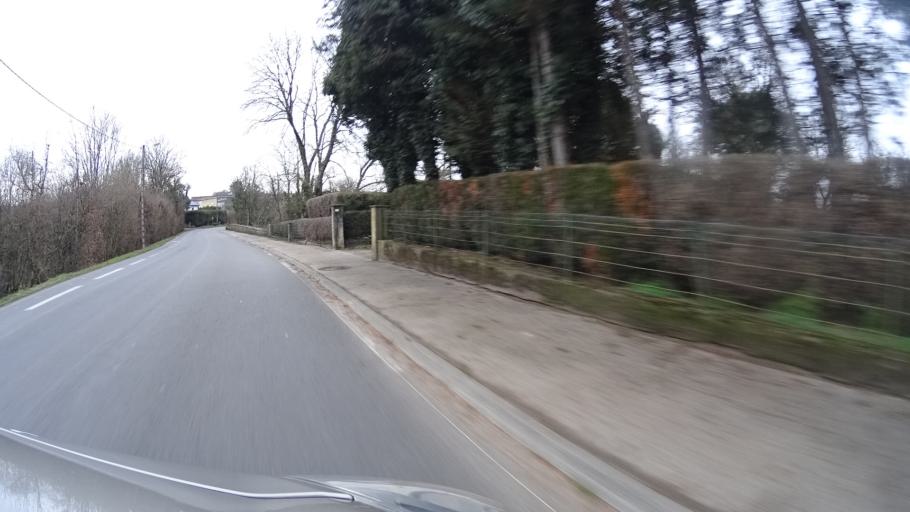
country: FR
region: Franche-Comte
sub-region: Departement du Doubs
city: Saone
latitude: 47.2160
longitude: 6.1084
